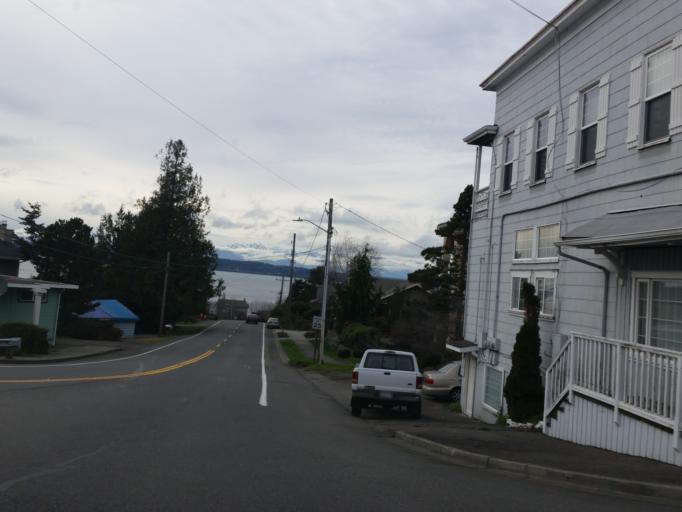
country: US
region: Washington
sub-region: Snohomish County
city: Woodway
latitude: 47.7718
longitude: -122.3885
